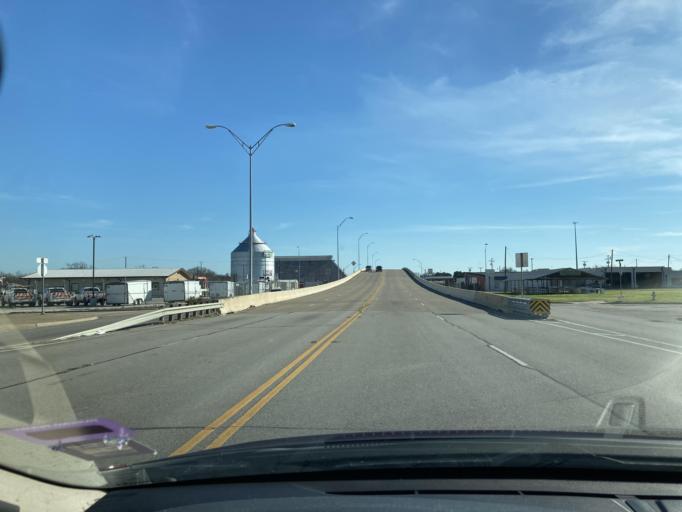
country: US
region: Texas
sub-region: Navarro County
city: Corsicana
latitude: 32.0956
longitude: -96.4604
